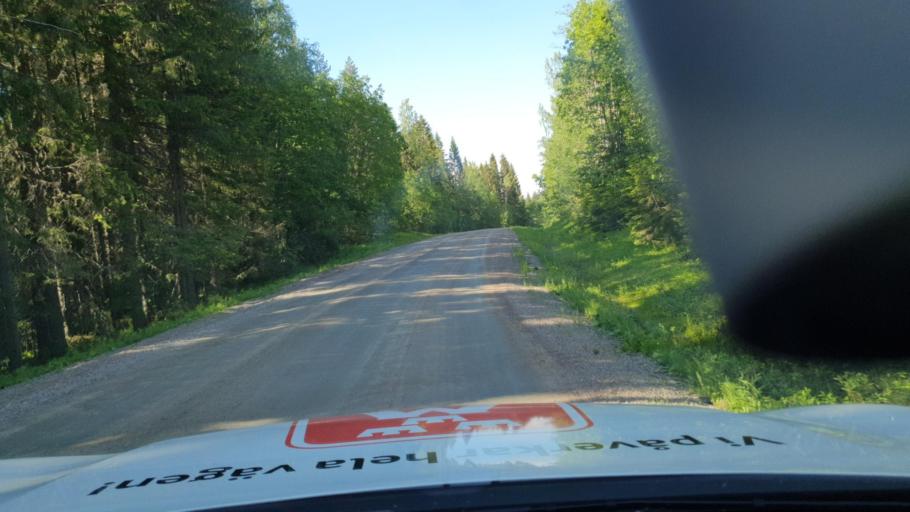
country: SE
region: Vaesterbotten
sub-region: Vannas Kommun
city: Vaennaes
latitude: 63.8454
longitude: 19.6219
